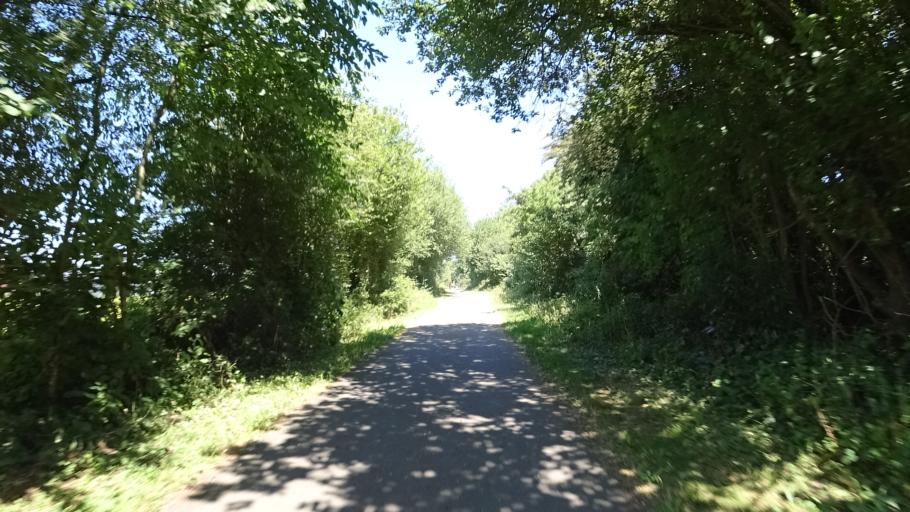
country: BE
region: Wallonia
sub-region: Province de Namur
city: Gembloux
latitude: 50.5842
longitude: 4.7155
